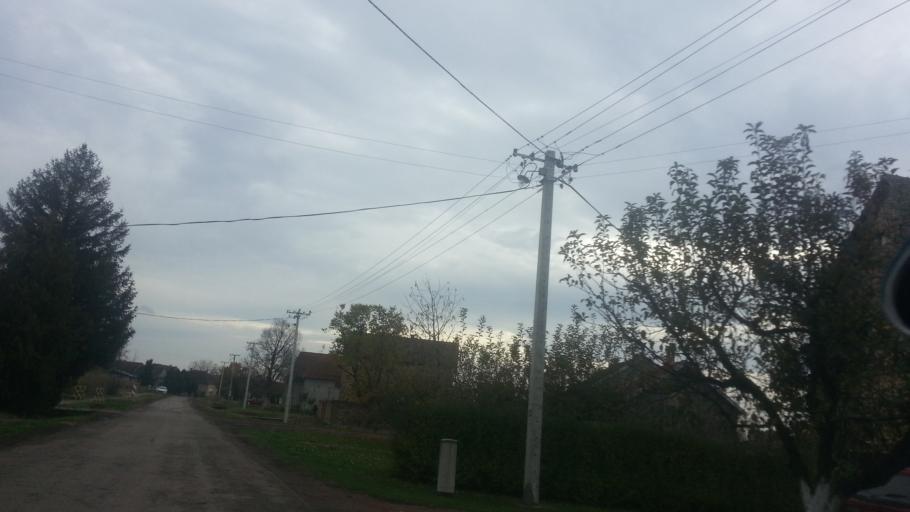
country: RS
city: Golubinci
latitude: 44.9894
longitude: 20.0582
